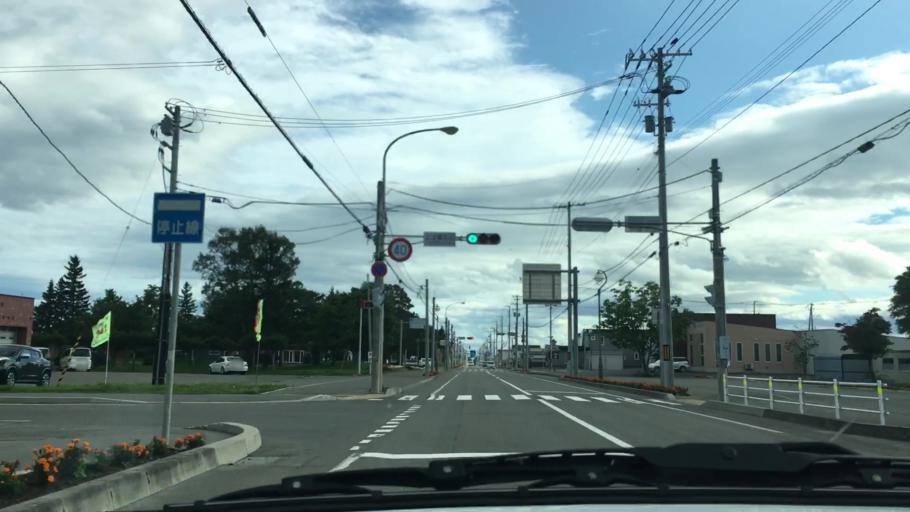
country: JP
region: Hokkaido
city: Otofuke
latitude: 43.2332
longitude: 143.2952
